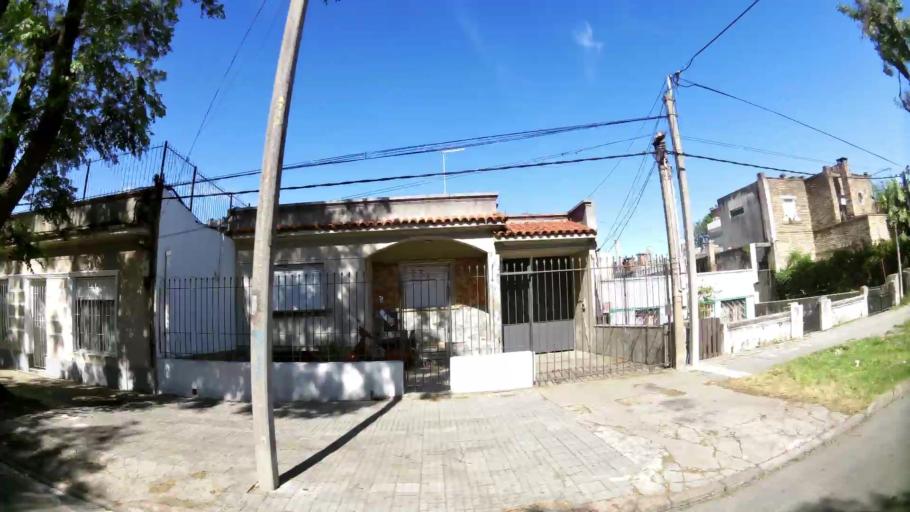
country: UY
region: Montevideo
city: Montevideo
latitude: -34.8923
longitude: -56.1417
